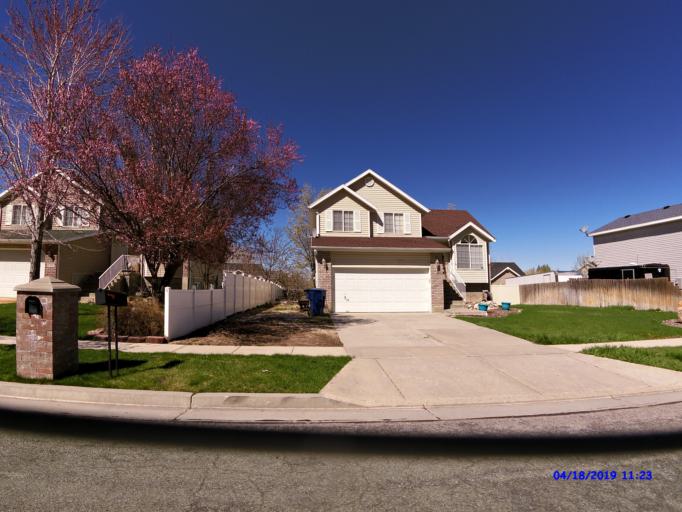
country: US
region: Utah
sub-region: Weber County
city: North Ogden
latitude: 41.2819
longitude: -111.9547
